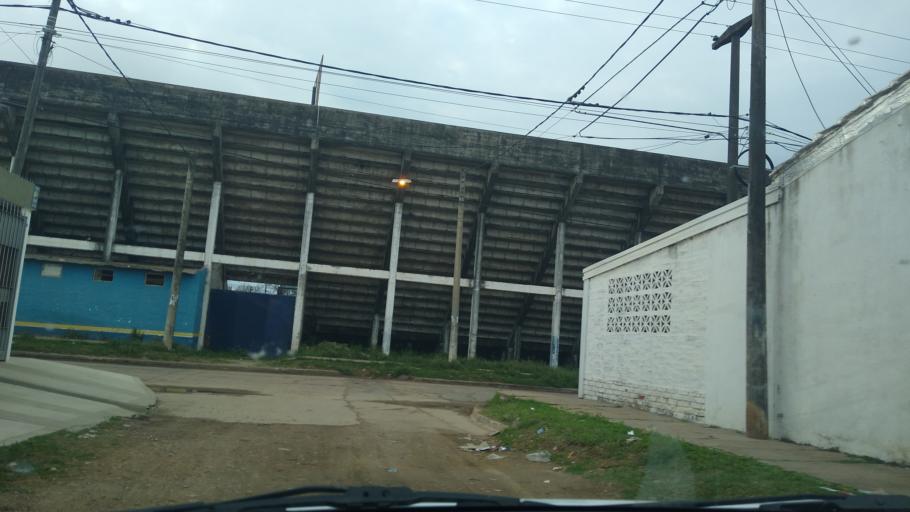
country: AR
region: Chaco
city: Barranqueras
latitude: -27.4849
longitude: -58.9265
